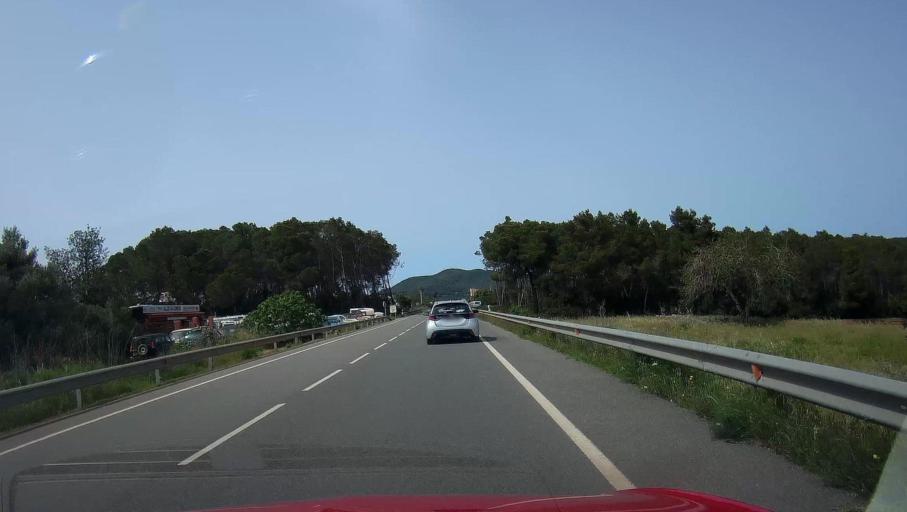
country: ES
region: Balearic Islands
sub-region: Illes Balears
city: Sant Joan de Labritja
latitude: 39.0426
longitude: 1.4920
